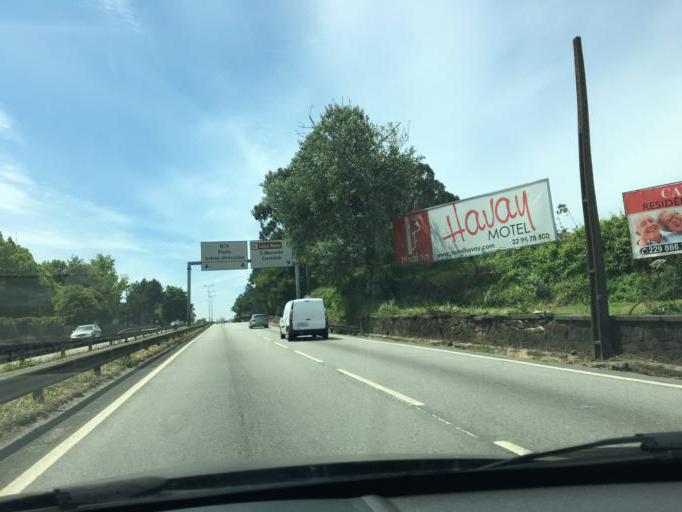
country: PT
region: Porto
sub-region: Maia
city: Leca do Bailio
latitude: 41.2139
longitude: -8.6271
